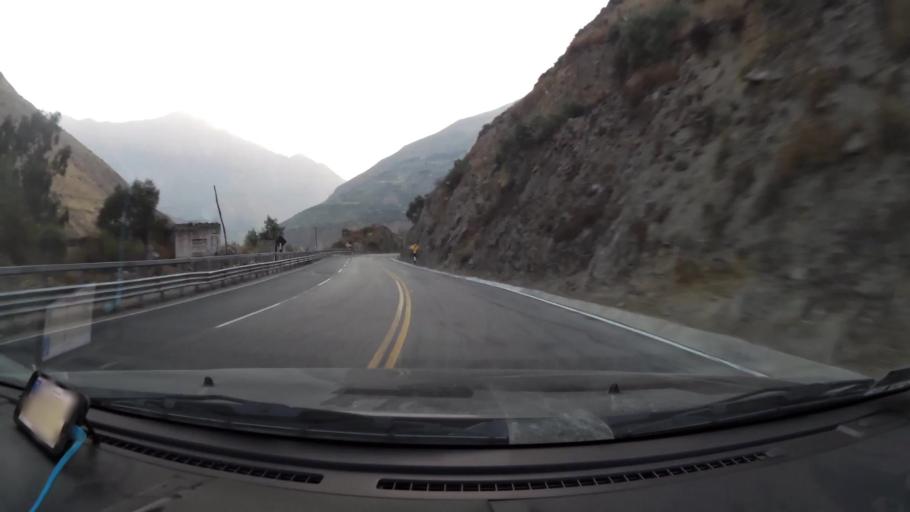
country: PE
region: Lima
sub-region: Provincia de Huarochiri
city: Matucana
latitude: -11.8587
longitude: -76.4163
